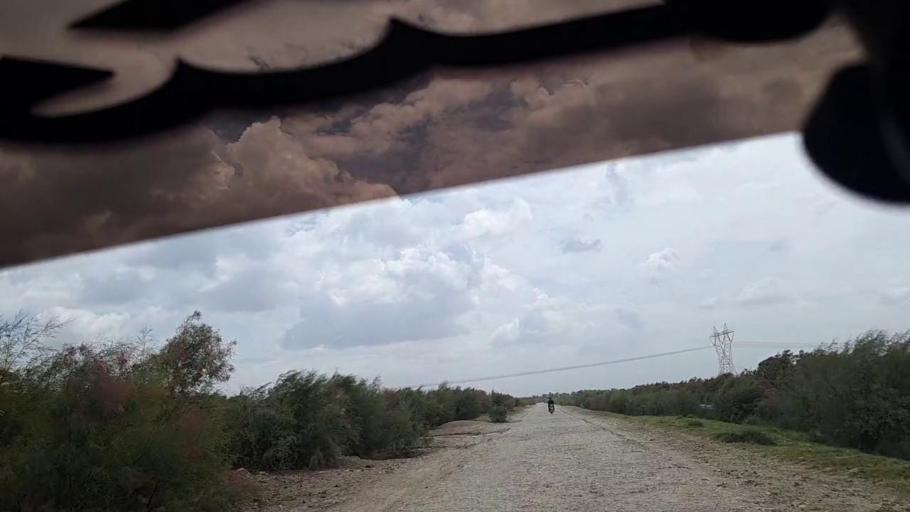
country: PK
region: Sindh
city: Ghauspur
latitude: 28.0677
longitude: 68.9383
